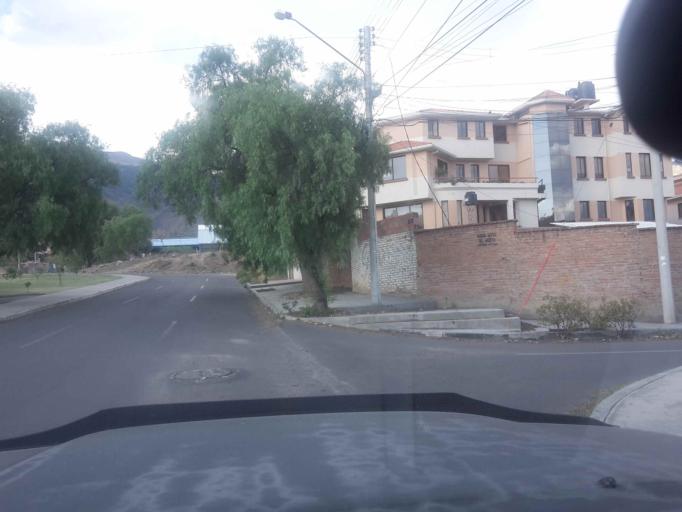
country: BO
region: Cochabamba
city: Cochabamba
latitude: -17.3572
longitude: -66.1687
